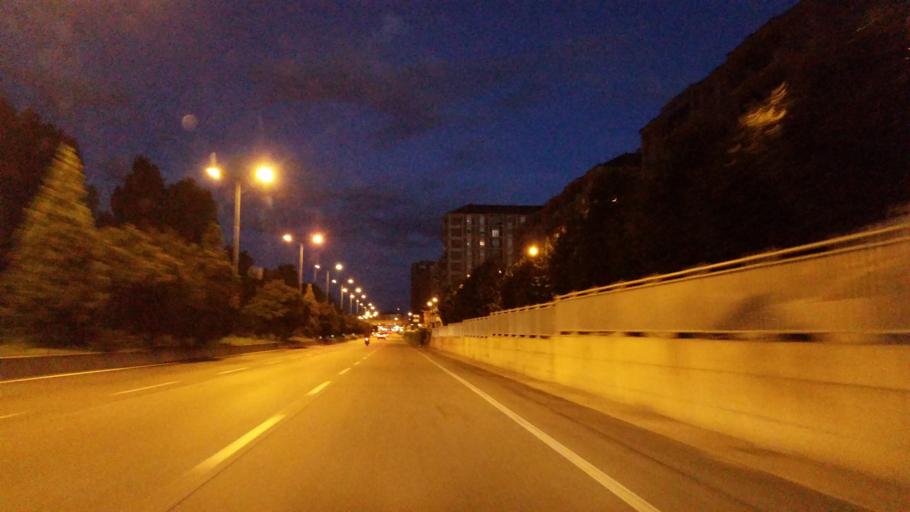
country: IT
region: Piedmont
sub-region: Provincia di Torino
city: Moncalieri
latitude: 45.0121
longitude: 7.6699
